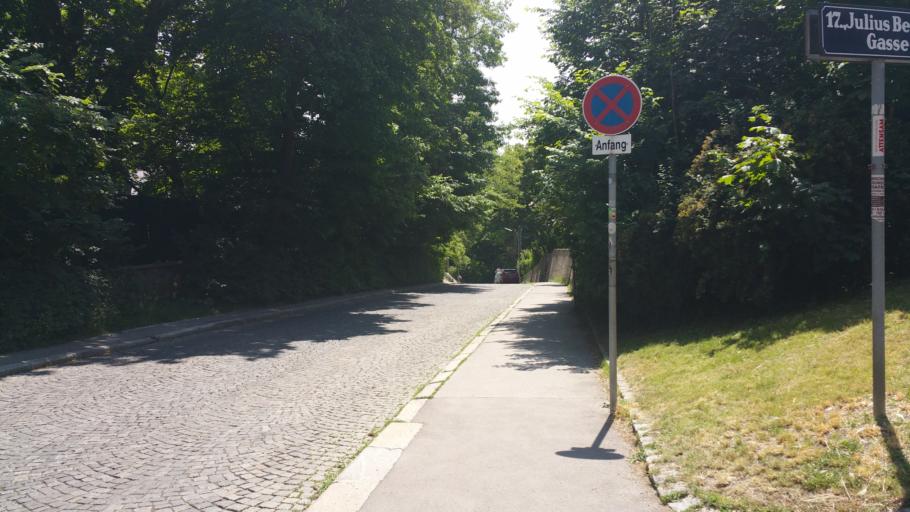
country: AT
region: Lower Austria
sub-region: Politischer Bezirk Wien-Umgebung
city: Klosterneuburg
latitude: 48.2352
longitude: 16.2871
